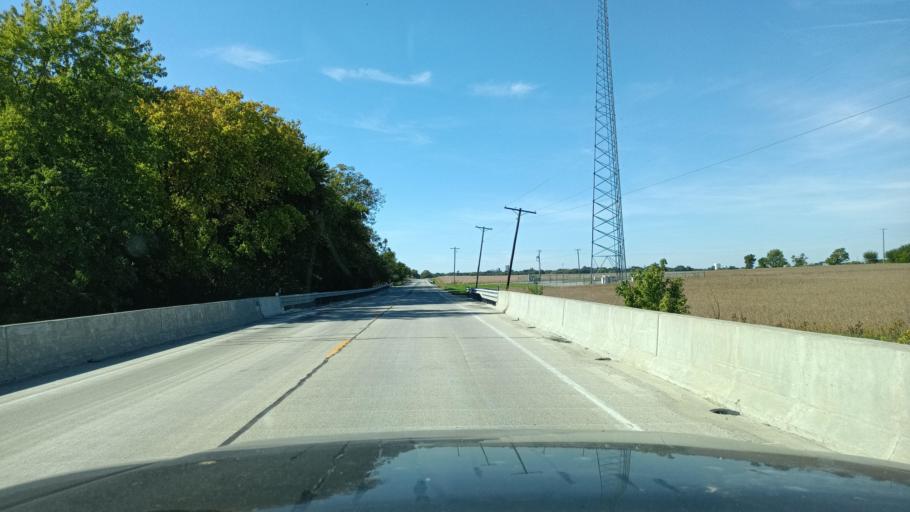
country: US
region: Illinois
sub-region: De Witt County
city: Farmer City
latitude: 40.2363
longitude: -88.6061
